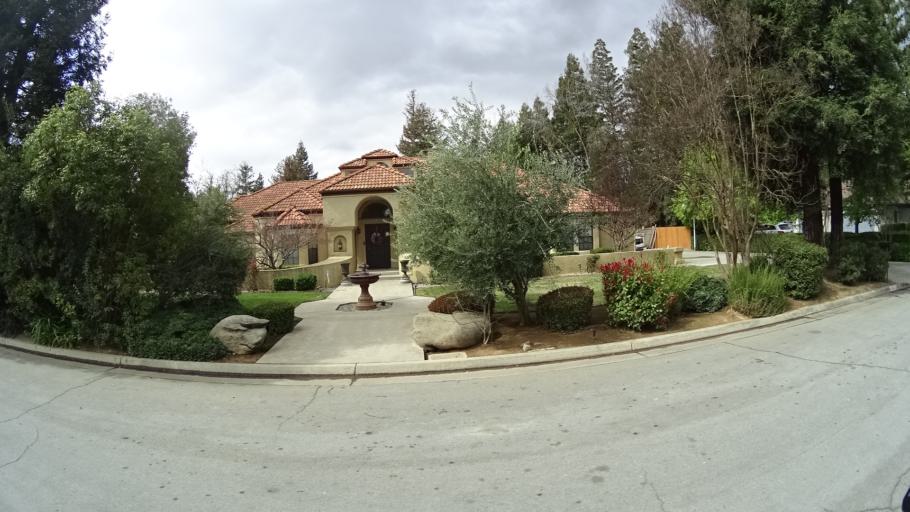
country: US
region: California
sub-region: Fresno County
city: Fresno
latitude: 36.8320
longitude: -119.8293
